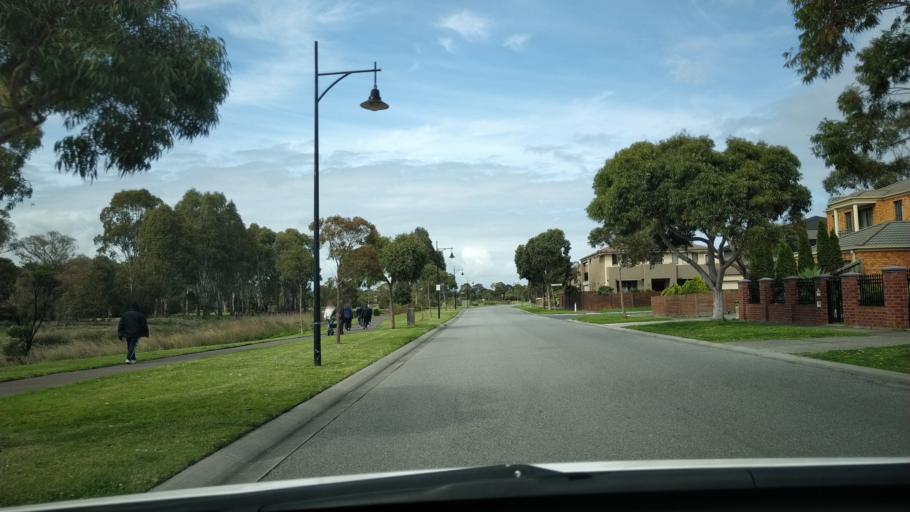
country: AU
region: Victoria
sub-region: Greater Dandenong
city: Keysborough
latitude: -37.9983
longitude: 145.1519
